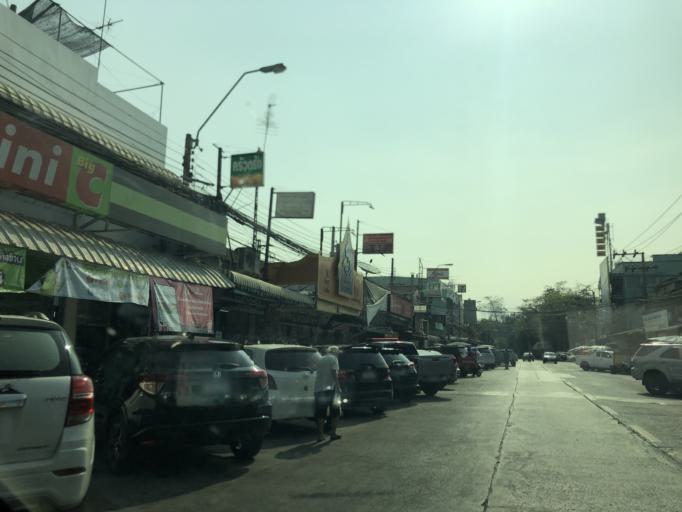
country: TH
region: Bangkok
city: Lak Si
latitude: 13.8741
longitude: 100.5797
